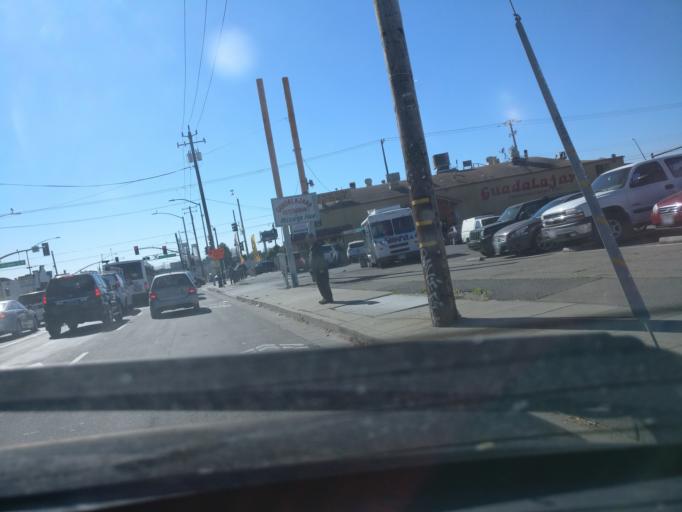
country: US
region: California
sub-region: Alameda County
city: Alameda
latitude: 37.7759
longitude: -122.2268
